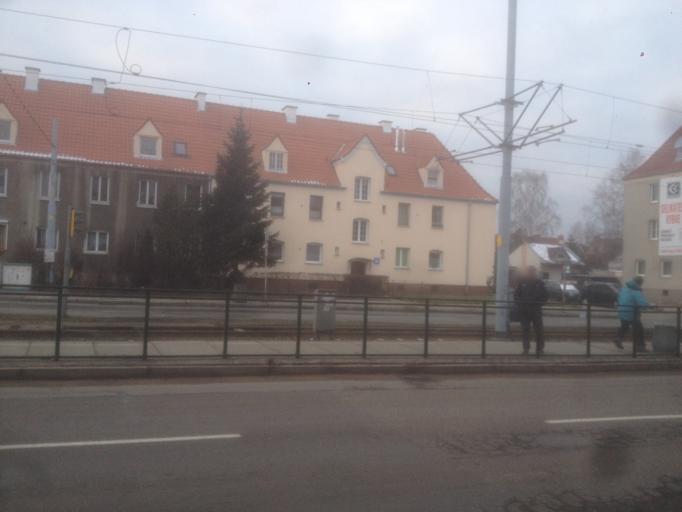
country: PL
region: Pomeranian Voivodeship
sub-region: Gdansk
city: Gdansk
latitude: 54.3837
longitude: 18.6221
